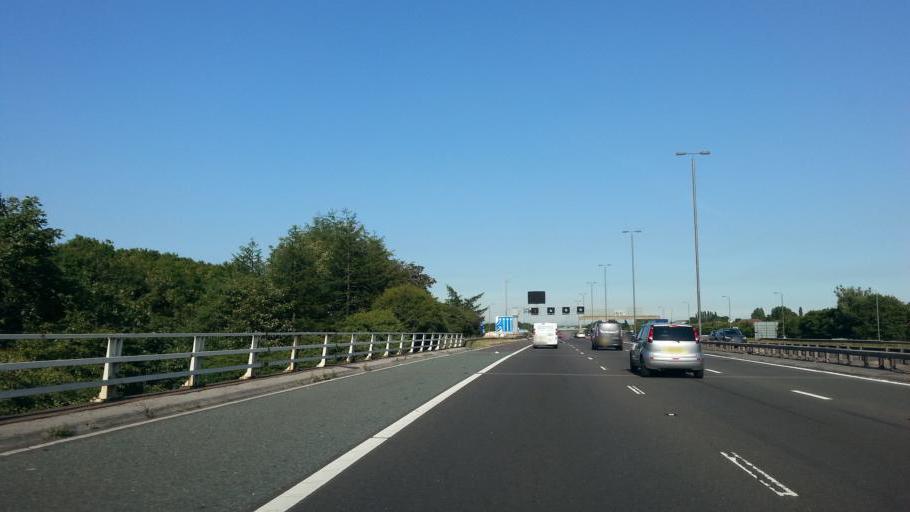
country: GB
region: England
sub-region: City and Borough of Leeds
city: Morley
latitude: 53.7336
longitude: -1.5756
